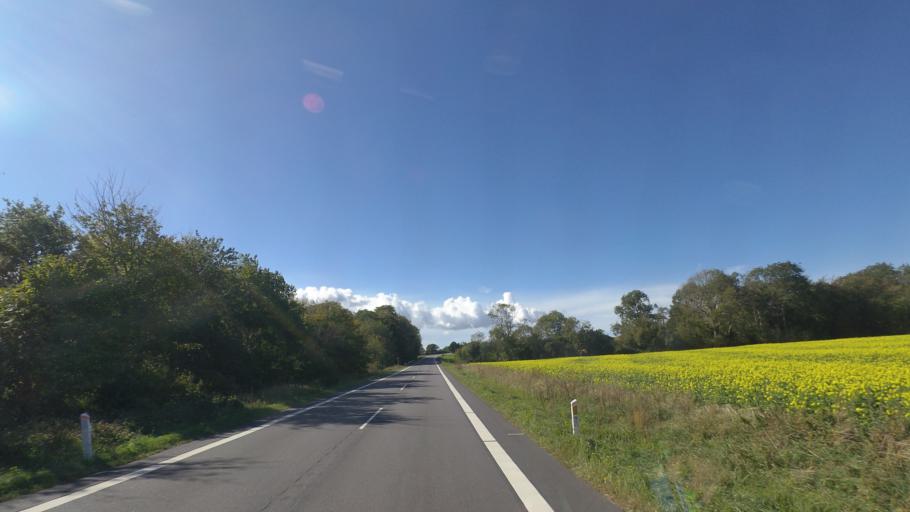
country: DK
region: Capital Region
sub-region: Bornholm Kommune
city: Akirkeby
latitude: 55.0692
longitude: 14.9797
